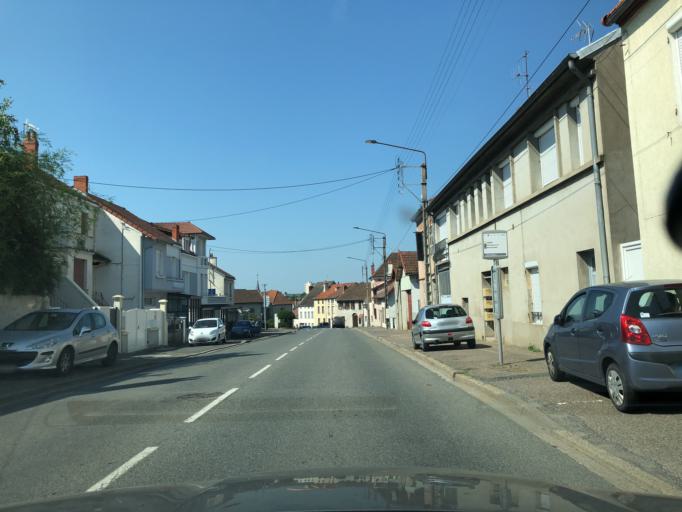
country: FR
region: Auvergne
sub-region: Departement de l'Allier
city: Cusset
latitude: 46.1353
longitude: 3.4634
